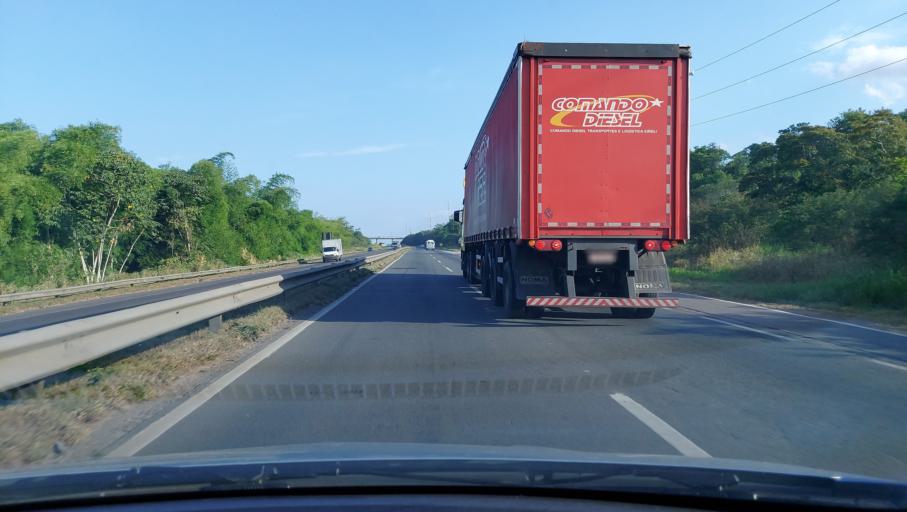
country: BR
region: Bahia
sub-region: Conceicao Do Jacuipe
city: Conceicao do Jacuipe
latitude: -12.3560
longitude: -38.8296
